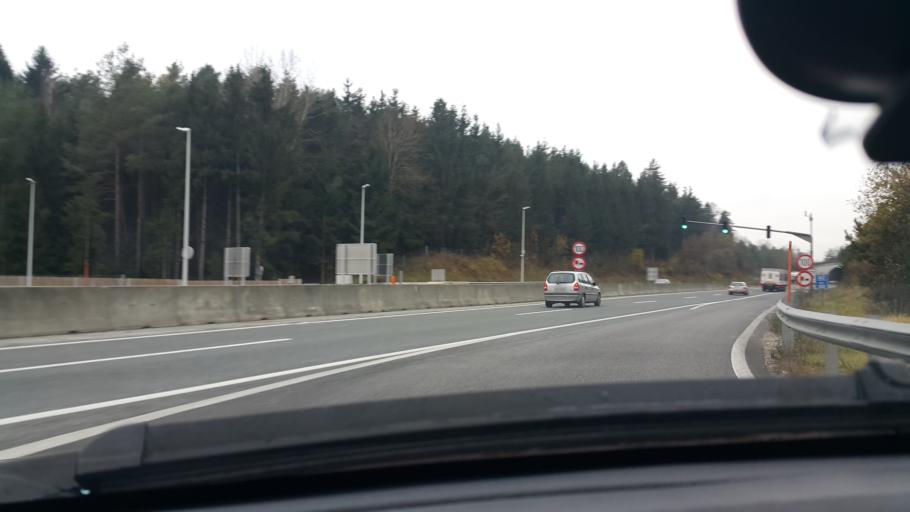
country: AT
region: Carinthia
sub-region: Politischer Bezirk Klagenfurt Land
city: Poggersdorf
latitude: 46.6403
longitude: 14.4368
